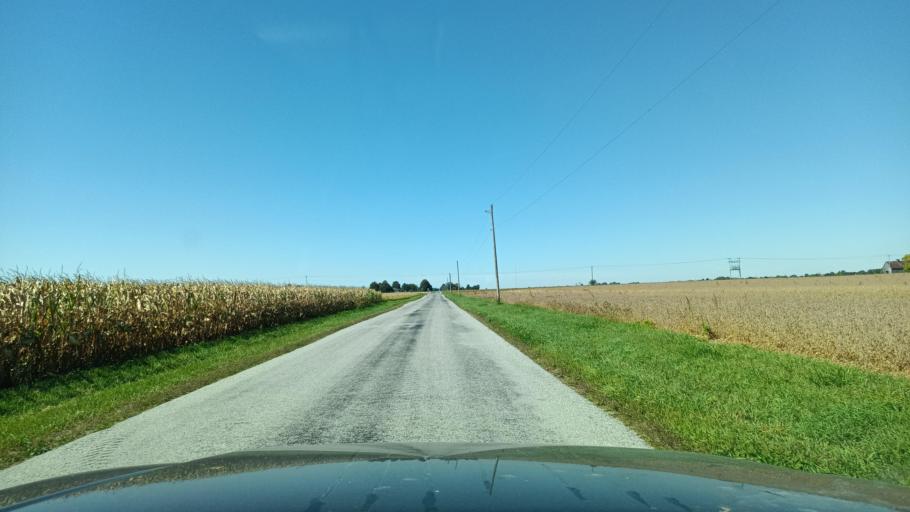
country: US
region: Illinois
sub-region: Champaign County
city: Mahomet
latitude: 40.0987
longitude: -88.3655
